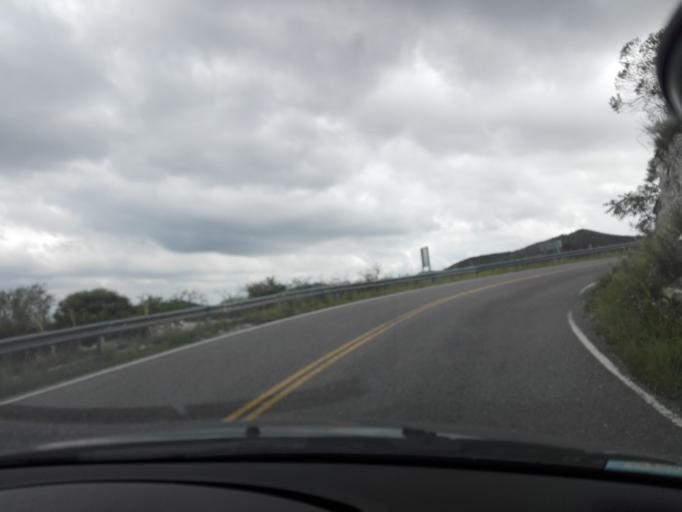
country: AR
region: Cordoba
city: Alta Gracia
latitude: -31.5913
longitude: -64.5124
